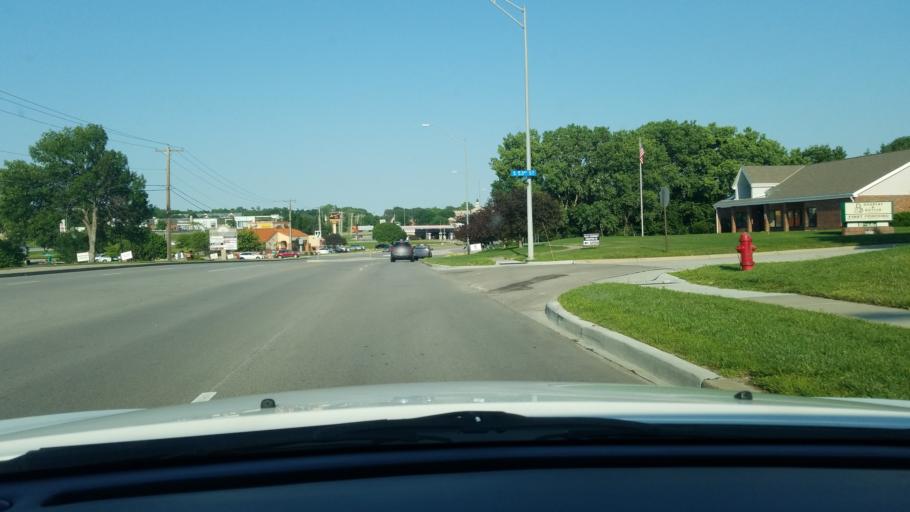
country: US
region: Nebraska
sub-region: Lancaster County
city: Lincoln
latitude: 40.7552
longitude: -96.6475
